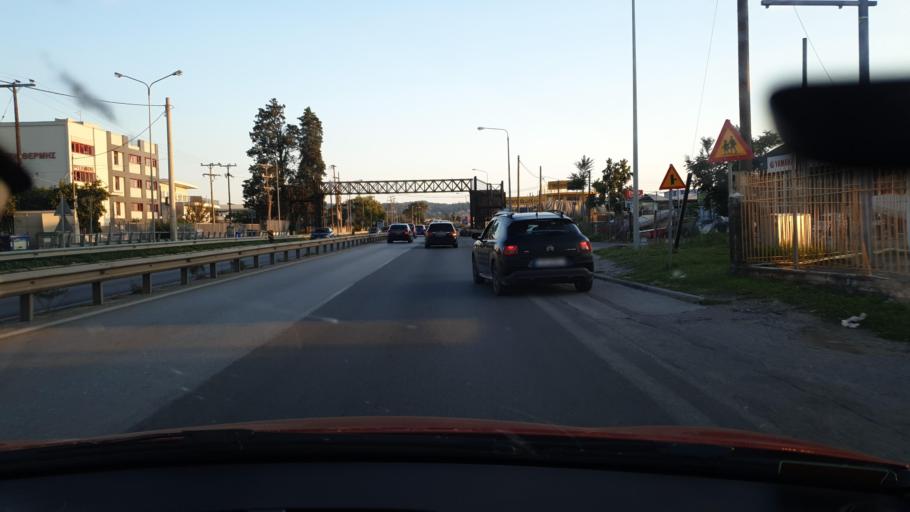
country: GR
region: Central Macedonia
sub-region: Nomos Thessalonikis
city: Neo Rysi
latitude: 40.5246
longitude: 22.9946
